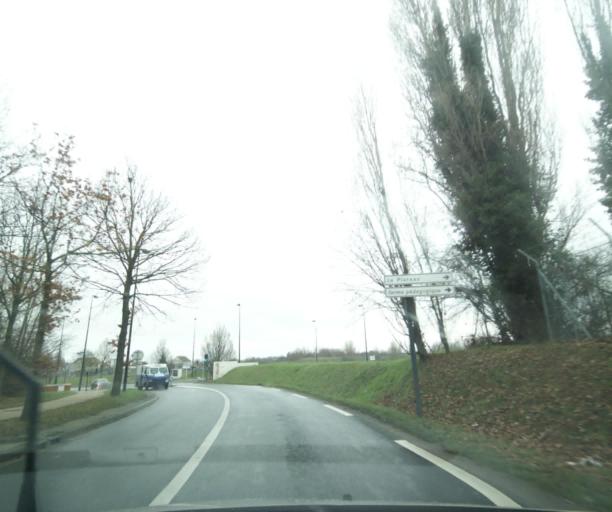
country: FR
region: Ile-de-France
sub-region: Departement du Val-de-Marne
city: Villeneuve-le-Roi
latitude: 48.7332
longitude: 2.4028
